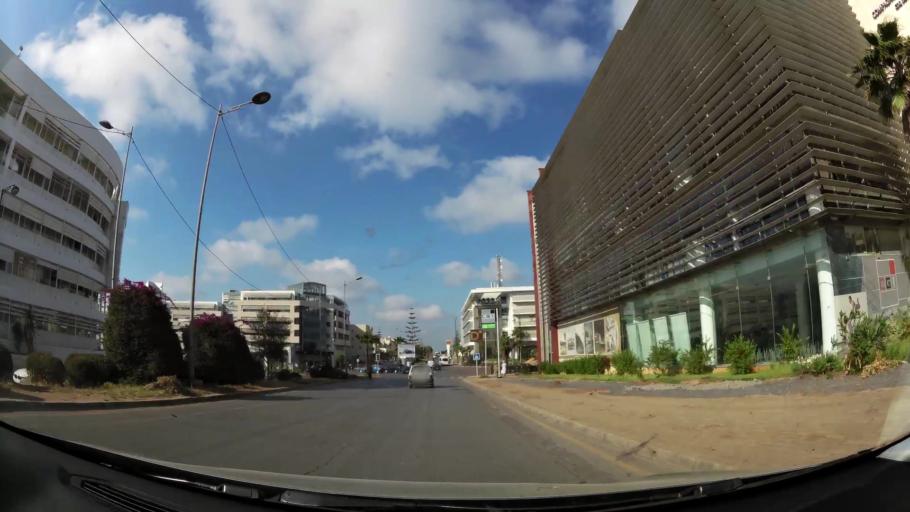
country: MA
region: Rabat-Sale-Zemmour-Zaer
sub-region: Skhirate-Temara
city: Temara
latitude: 33.9529
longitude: -6.8647
